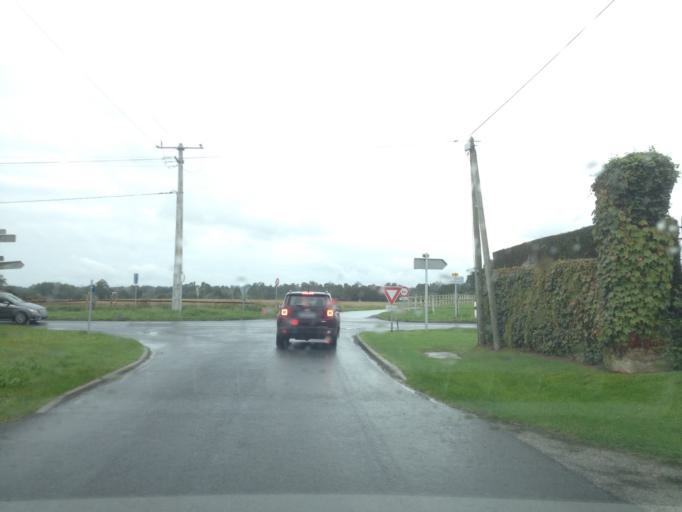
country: FR
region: Lower Normandy
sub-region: Departement du Calvados
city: Bayeux
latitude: 49.2993
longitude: -0.7312
